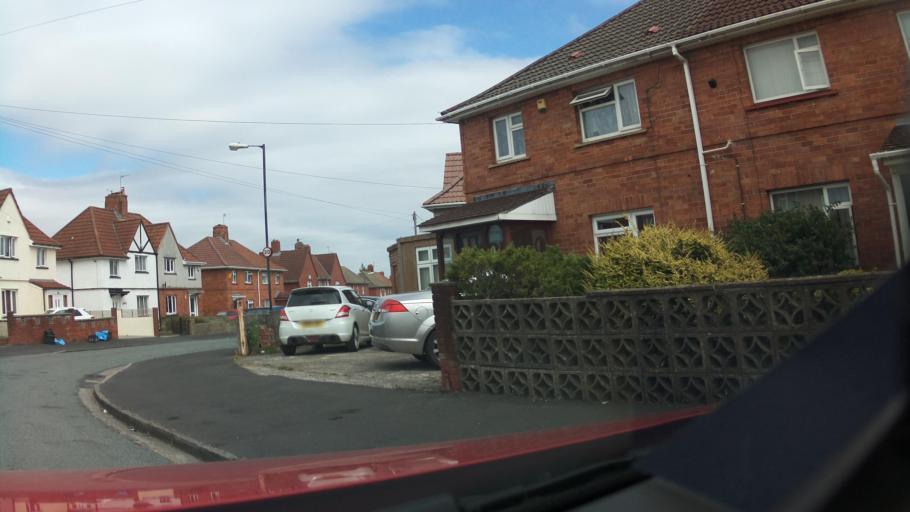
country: GB
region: England
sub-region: Bristol
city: Bristol
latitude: 51.4293
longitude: -2.5890
